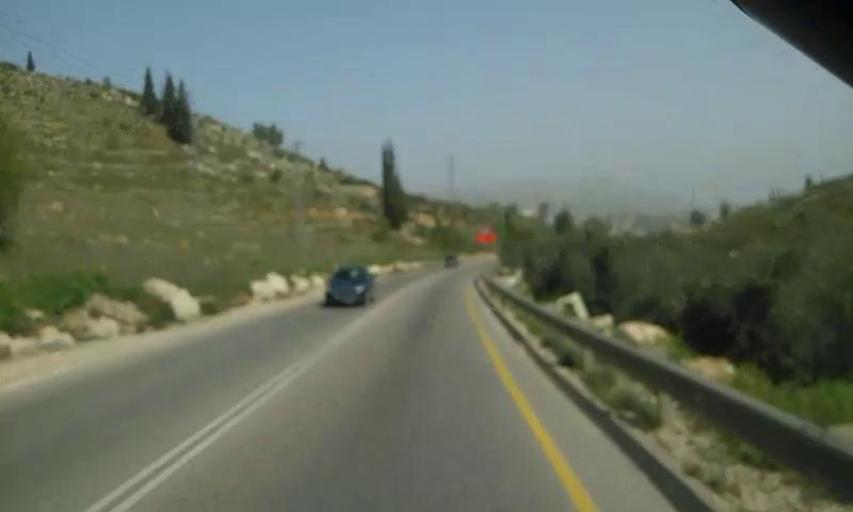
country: PS
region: West Bank
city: `Aynabus
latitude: 32.1279
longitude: 35.2570
